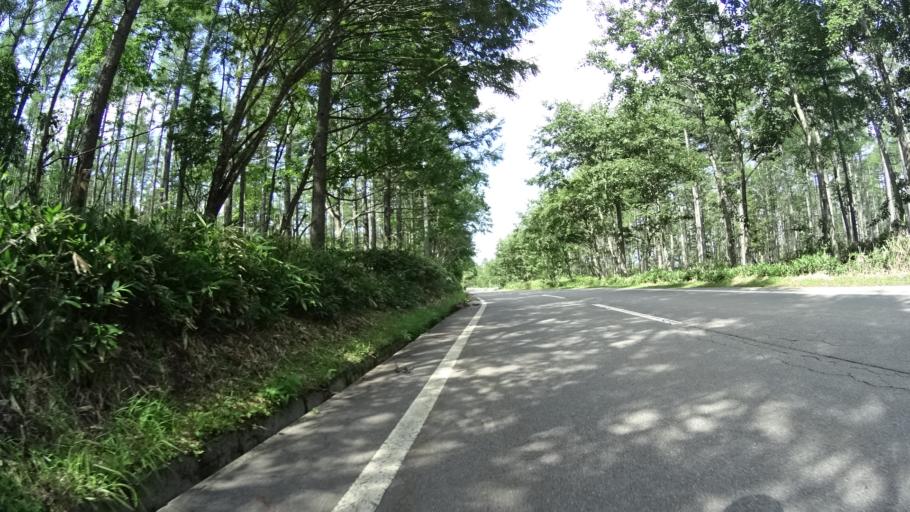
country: JP
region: Nagano
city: Saku
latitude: 36.0549
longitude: 138.3948
